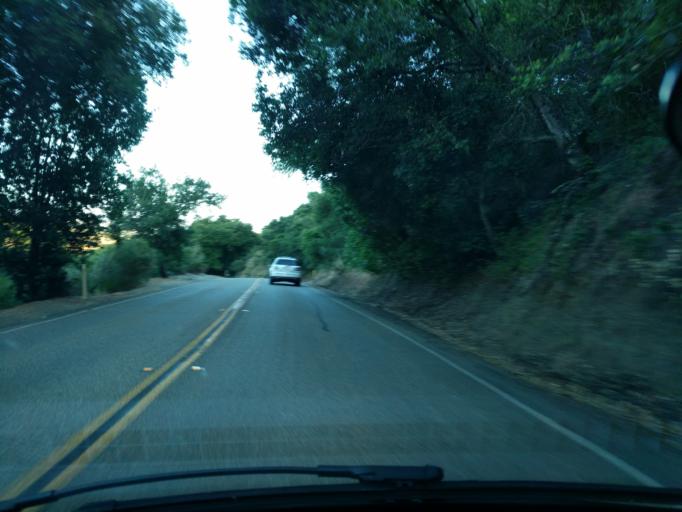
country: US
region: California
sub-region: Alameda County
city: Ashland
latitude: 37.7192
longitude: -122.1094
